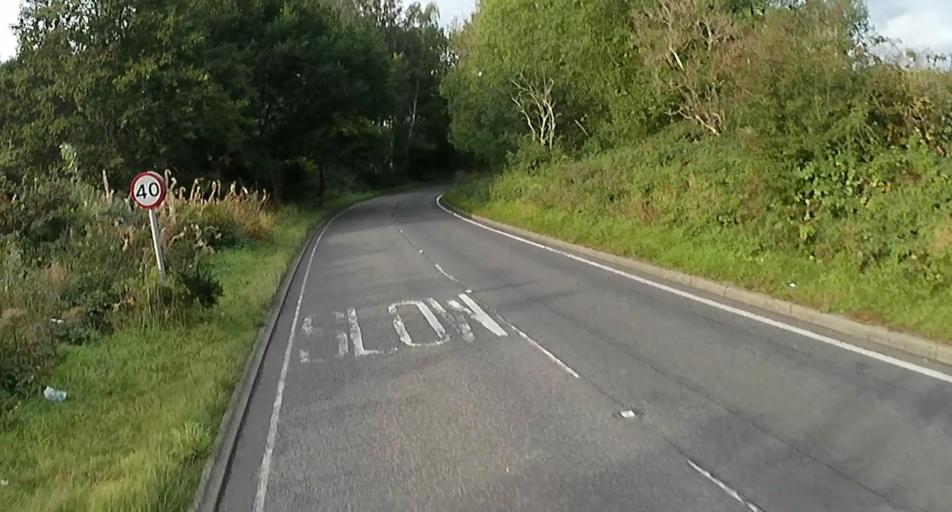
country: GB
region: England
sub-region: West Berkshire
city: Thatcham
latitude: 51.3819
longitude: -1.2490
